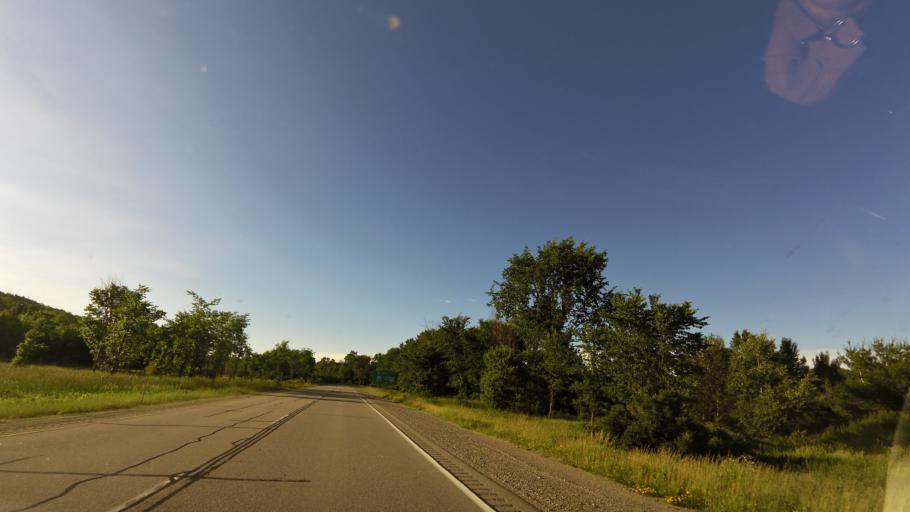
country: CA
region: Ontario
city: Midland
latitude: 44.6949
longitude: -79.6481
